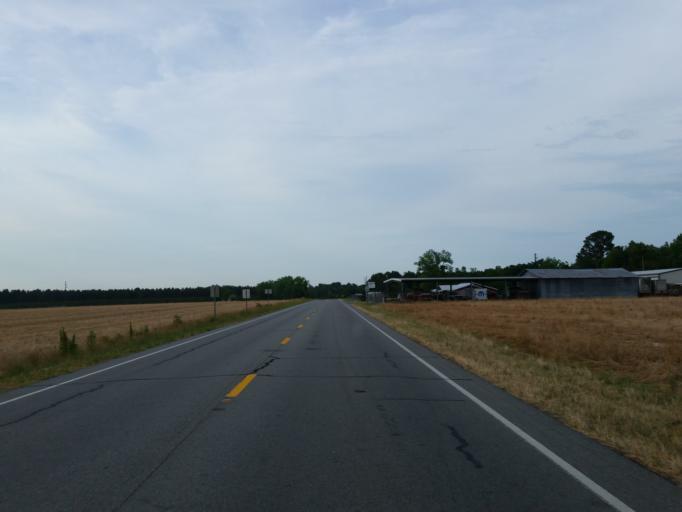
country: US
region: Georgia
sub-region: Dooly County
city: Unadilla
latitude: 32.2023
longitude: -83.7609
